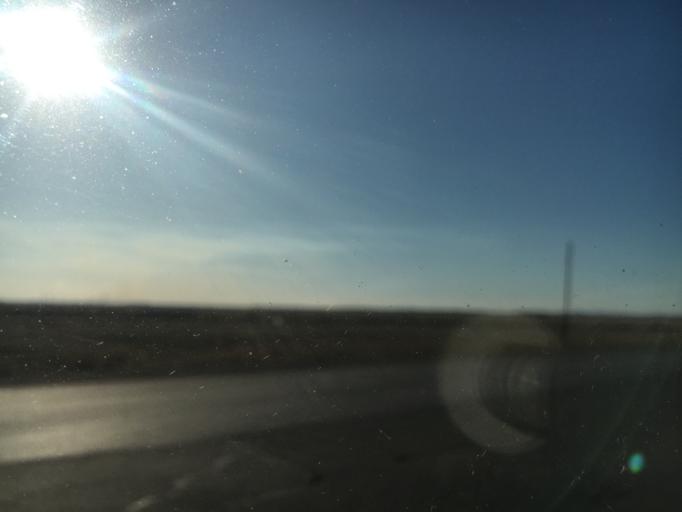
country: KZ
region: Qaraghandy
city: Tokarevka
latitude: 50.1199
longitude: 73.2112
